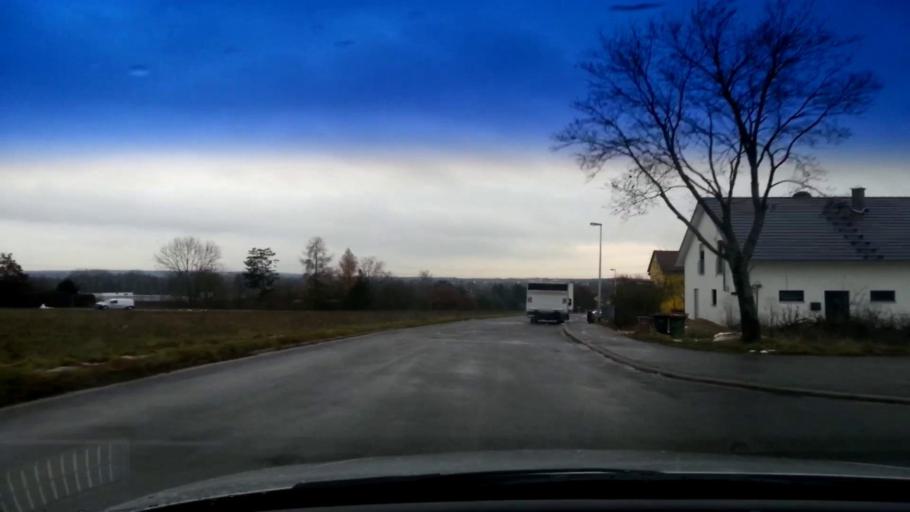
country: DE
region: Bavaria
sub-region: Upper Franconia
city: Gundelsheim
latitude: 49.9408
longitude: 10.9264
